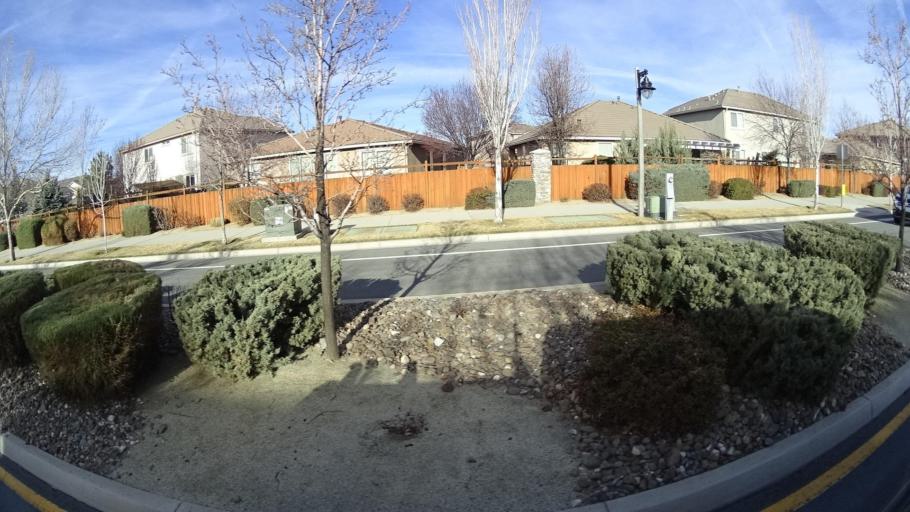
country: US
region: Nevada
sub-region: Washoe County
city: Spanish Springs
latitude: 39.6204
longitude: -119.6699
